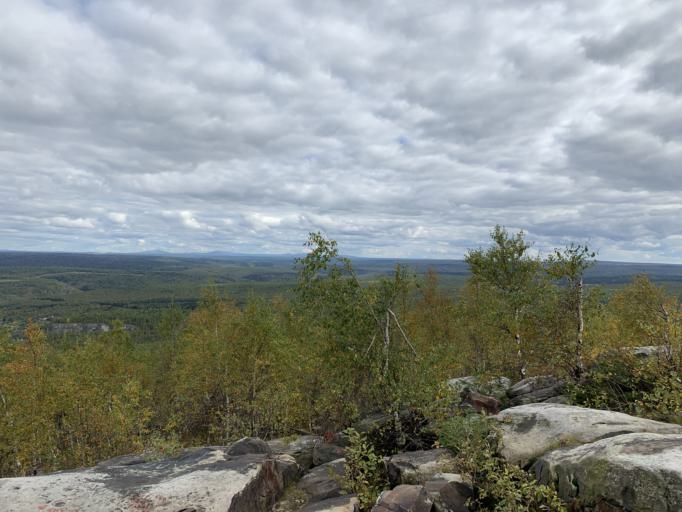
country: RU
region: Perm
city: Gubakha
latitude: 58.8534
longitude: 57.5819
